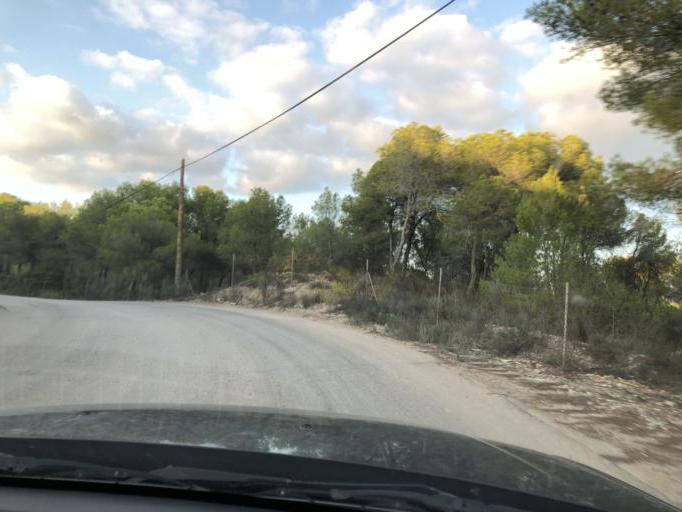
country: ES
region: Balearic Islands
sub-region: Illes Balears
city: Santa Ponsa
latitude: 39.5300
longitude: 2.4815
